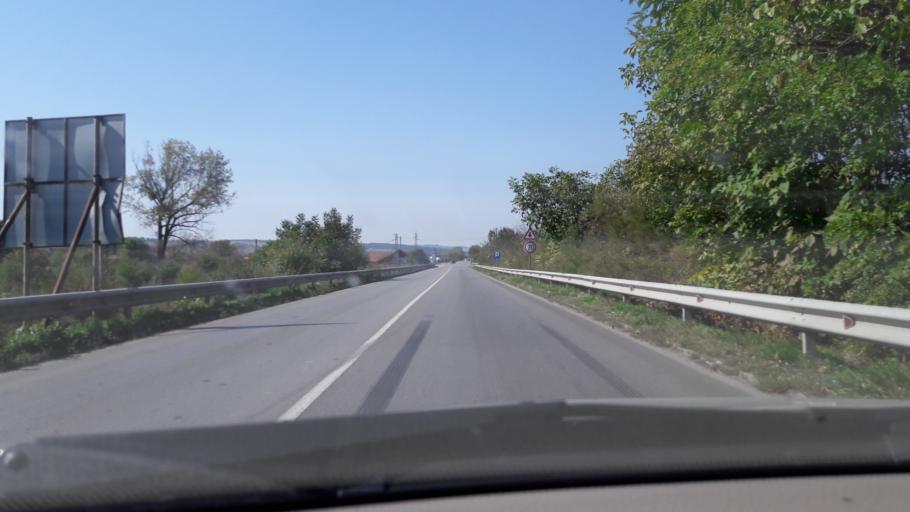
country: BG
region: Razgrad
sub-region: Obshtina Razgrad
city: Razgrad
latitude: 43.5478
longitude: 26.4818
